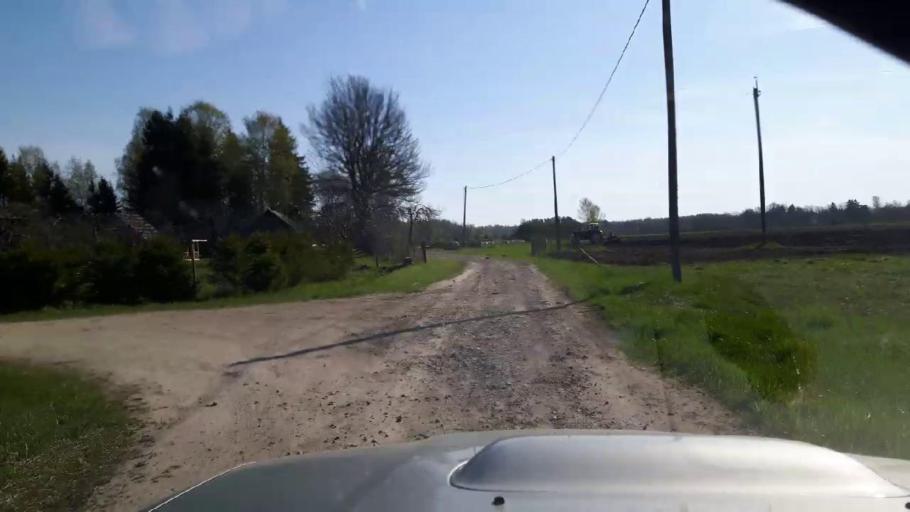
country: EE
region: Paernumaa
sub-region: Tootsi vald
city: Tootsi
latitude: 58.4916
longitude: 24.9081
